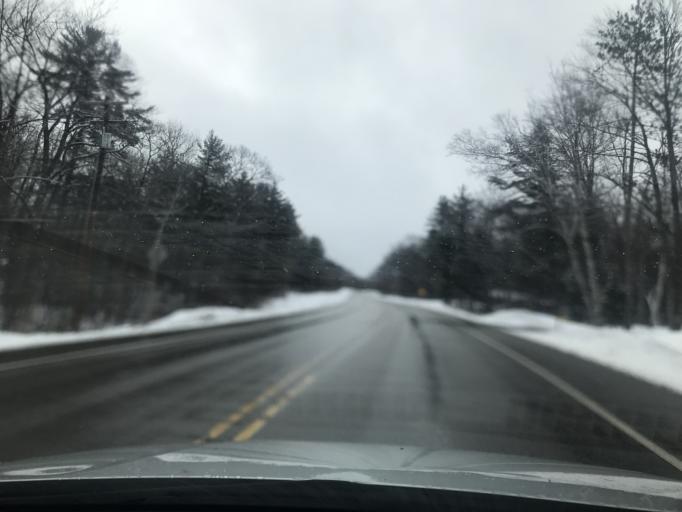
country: US
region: Wisconsin
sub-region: Marinette County
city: Peshtigo
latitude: 45.1704
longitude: -87.7356
